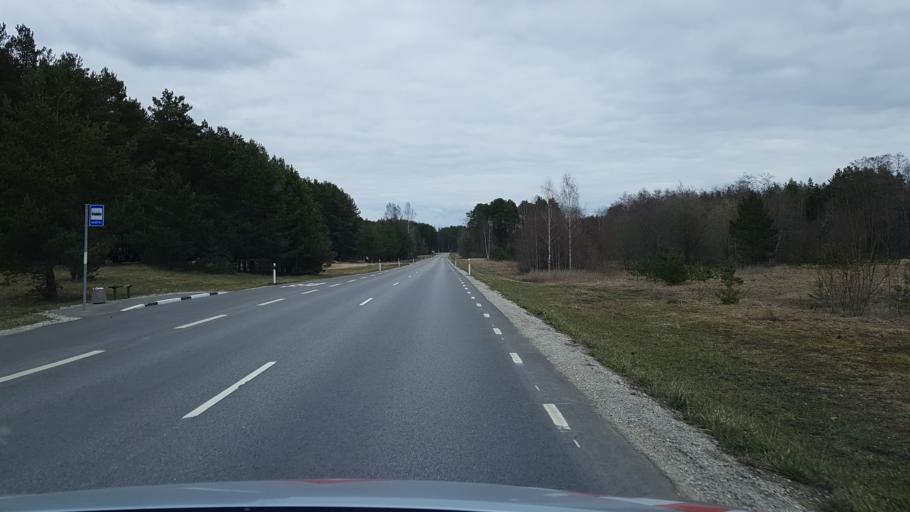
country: EE
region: Ida-Virumaa
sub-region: Narva-Joesuu linn
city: Narva-Joesuu
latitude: 59.4170
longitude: 28.0972
